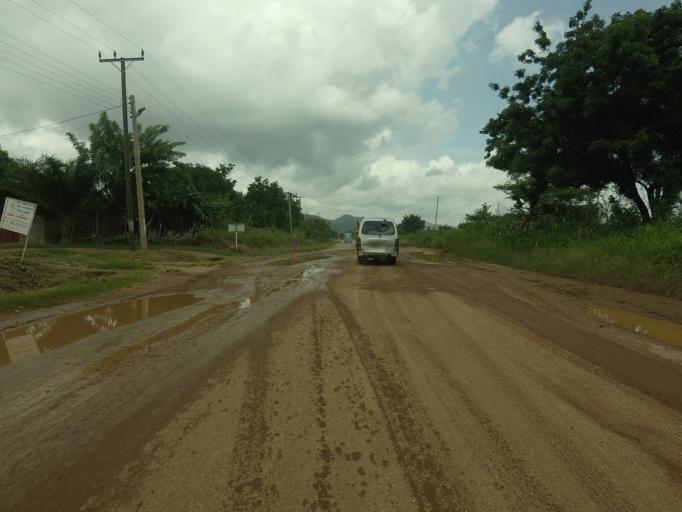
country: GH
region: Volta
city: Ho
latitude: 6.7069
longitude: 0.3343
